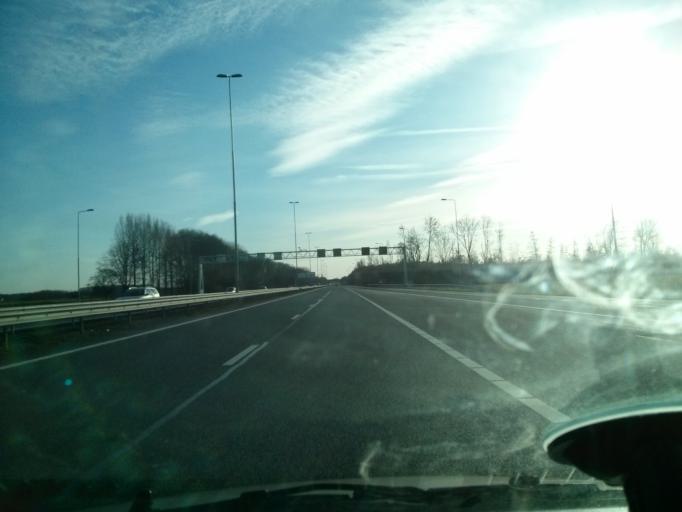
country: NL
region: Gelderland
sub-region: Gemeente Wijchen
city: Bergharen
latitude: 51.8534
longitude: 5.7058
